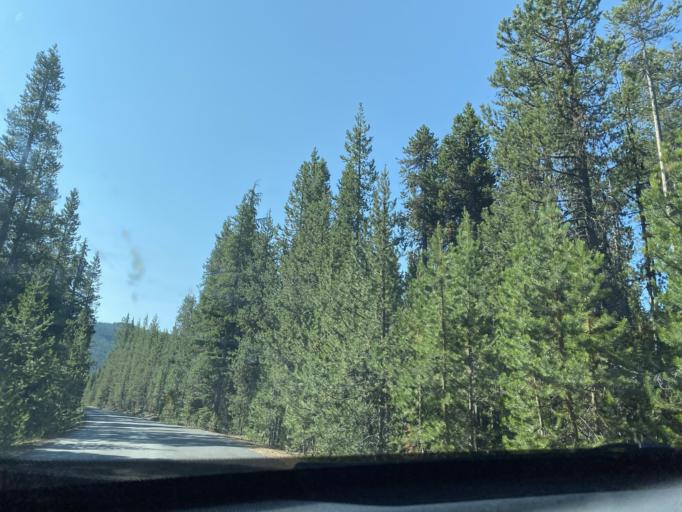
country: US
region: Oregon
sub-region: Deschutes County
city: Three Rivers
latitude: 43.7056
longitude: -121.2753
